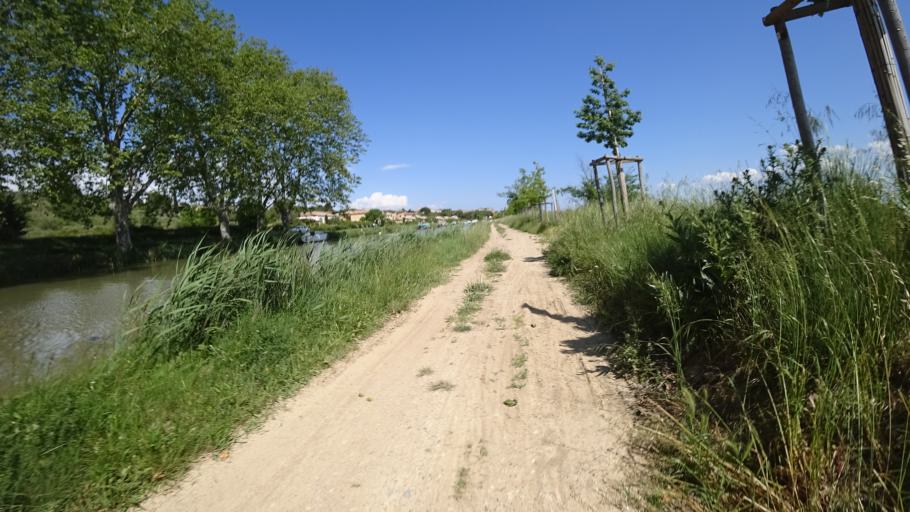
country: FR
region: Languedoc-Roussillon
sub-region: Departement de l'Aude
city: Canet
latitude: 43.2479
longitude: 2.8501
